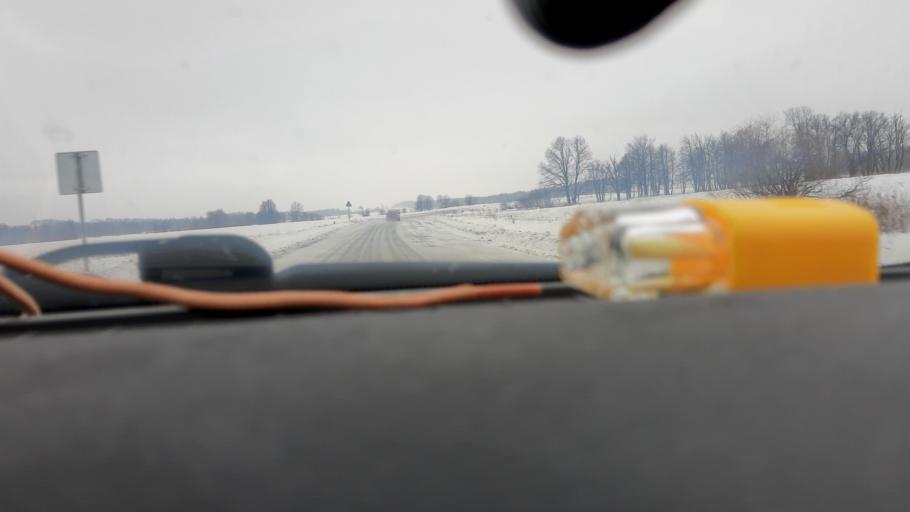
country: RU
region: Bashkortostan
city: Ulukulevo
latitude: 54.5901
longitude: 56.4262
